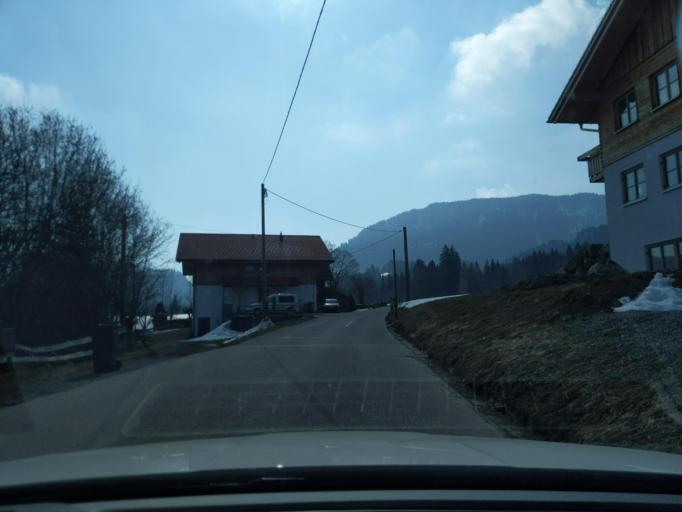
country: DE
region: Bavaria
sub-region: Swabia
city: Obermaiselstein
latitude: 47.4528
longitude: 10.2334
